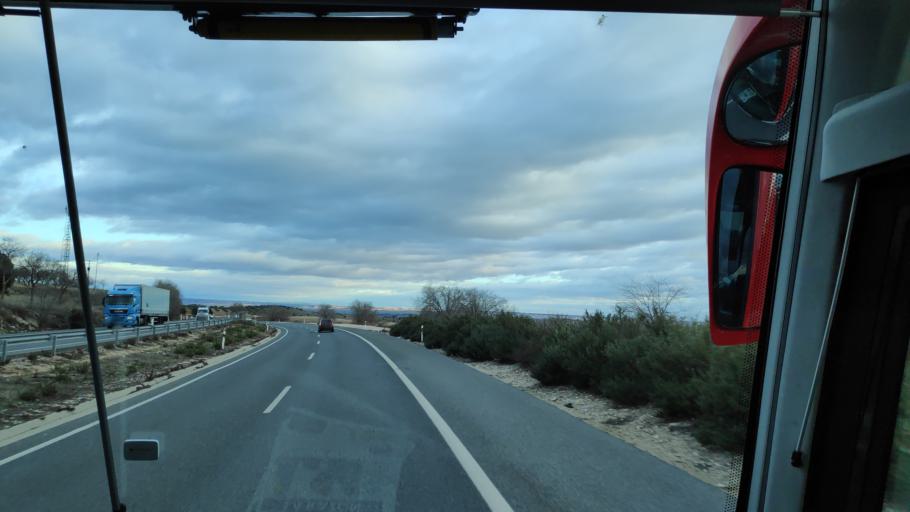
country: ES
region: Madrid
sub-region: Provincia de Madrid
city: Villarejo de Salvanes
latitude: 40.1536
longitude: -3.2501
